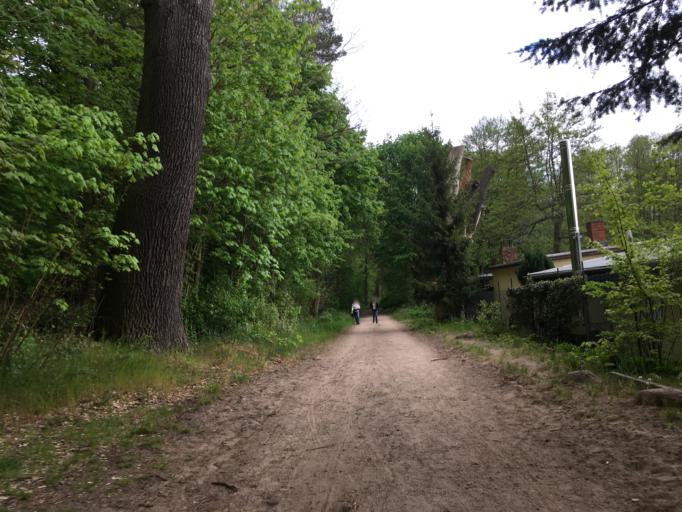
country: DE
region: Brandenburg
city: Rudnitz
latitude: 52.7523
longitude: 13.5954
